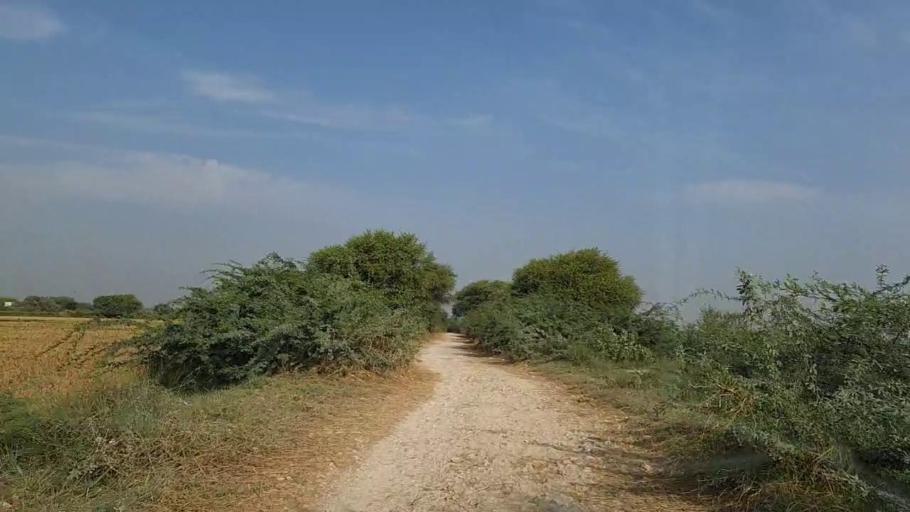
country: PK
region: Sindh
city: Mirpur Batoro
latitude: 24.7094
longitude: 68.2232
